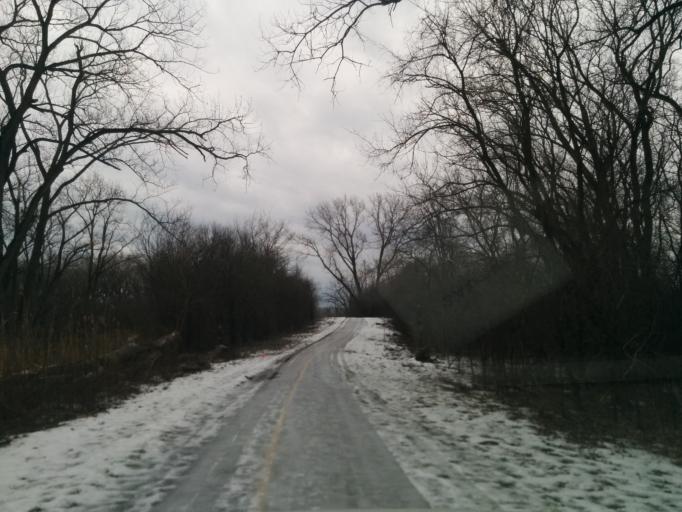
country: US
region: Illinois
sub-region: Cook County
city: Glencoe
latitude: 42.1315
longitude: -87.7770
